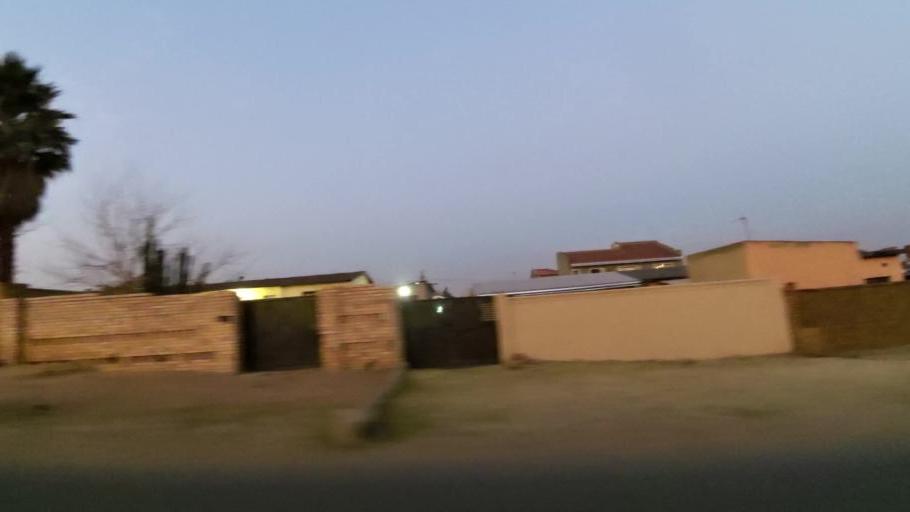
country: ZA
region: Gauteng
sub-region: City of Johannesburg Metropolitan Municipality
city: Soweto
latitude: -26.2295
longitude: 27.9116
